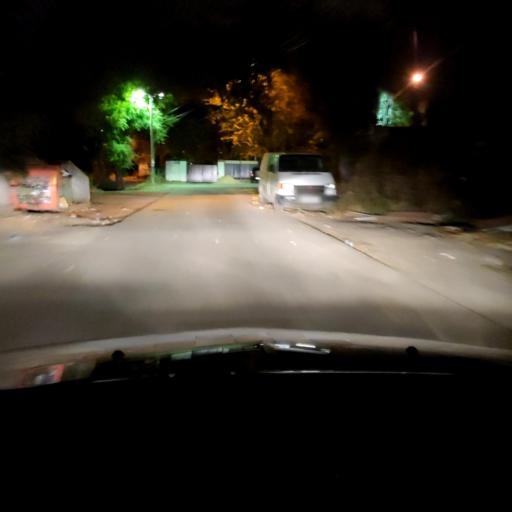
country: RU
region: Voronezj
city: Voronezh
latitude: 51.6279
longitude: 39.1789
